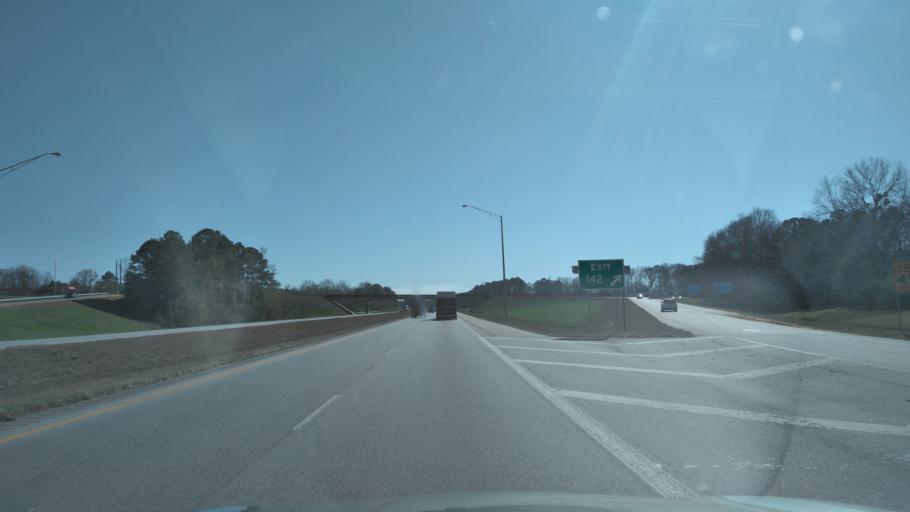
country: US
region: Alabama
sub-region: Lowndes County
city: Fort Deposit
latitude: 31.9877
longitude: -86.5285
